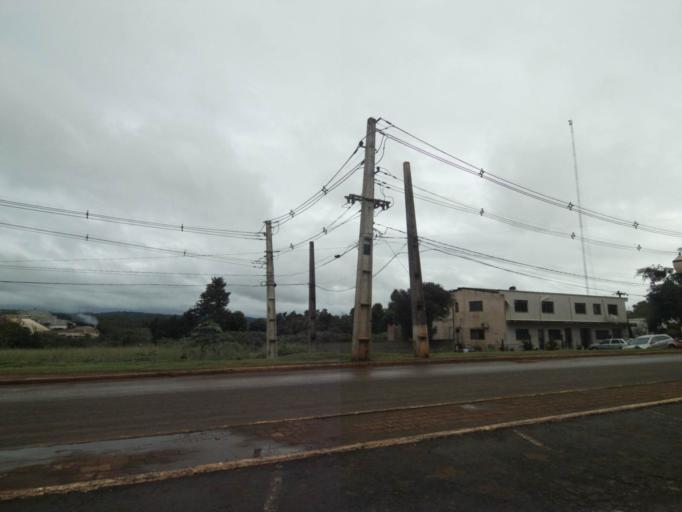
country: BR
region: Parana
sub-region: Marechal Candido Rondon
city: Marechal Candido Rondon
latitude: -24.5684
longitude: -54.0353
